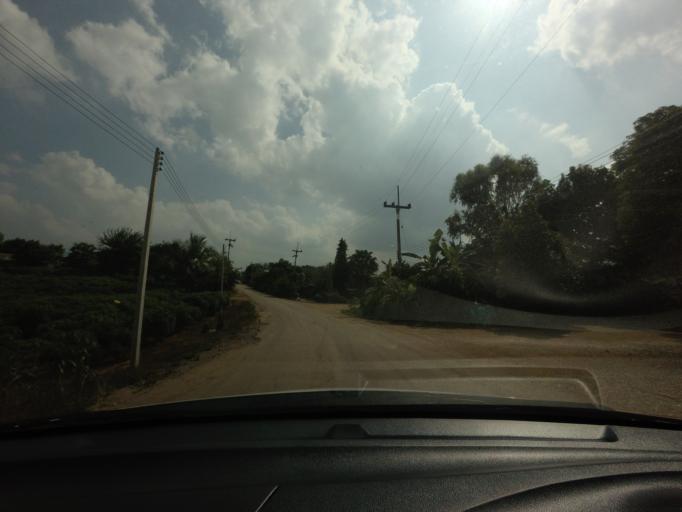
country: TH
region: Nakhon Ratchasima
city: Pak Chong
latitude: 14.5281
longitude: 101.5747
